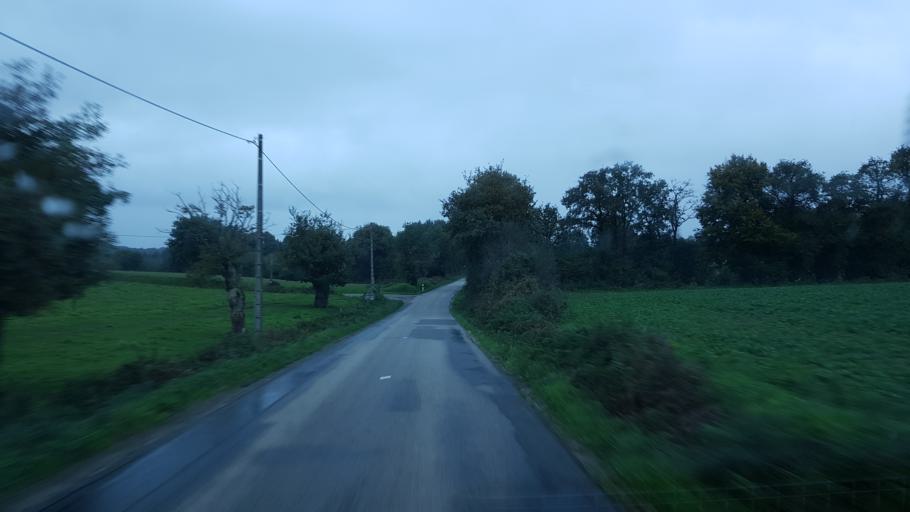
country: FR
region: Brittany
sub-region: Departement du Morbihan
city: Sulniac
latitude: 47.6880
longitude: -2.5719
